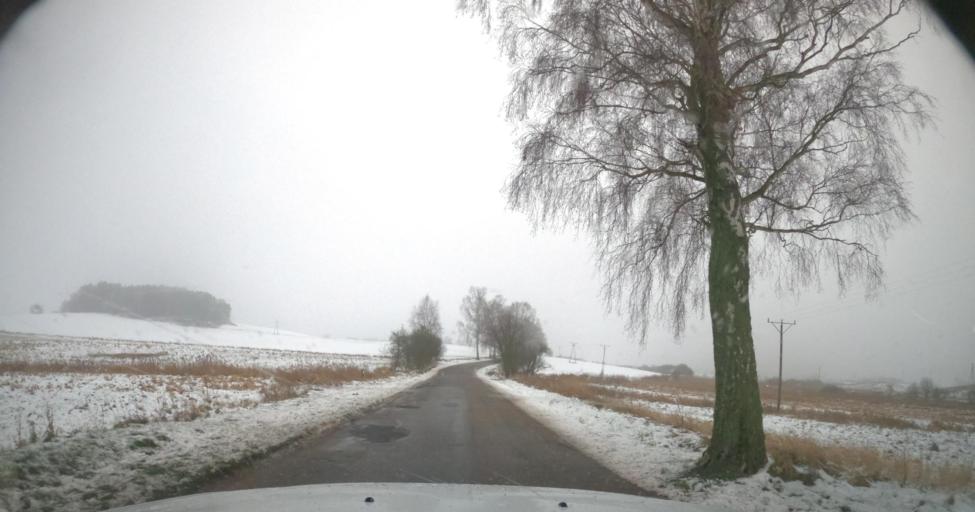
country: PL
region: West Pomeranian Voivodeship
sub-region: Powiat kamienski
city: Golczewo
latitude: 53.8674
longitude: 15.0831
